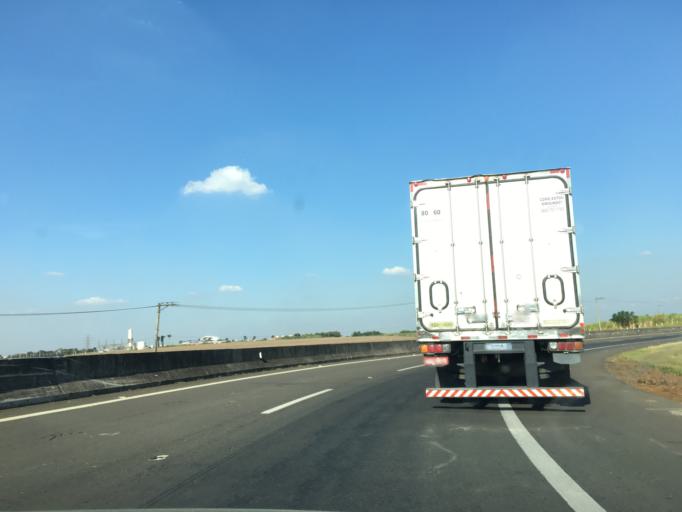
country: BR
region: Sao Paulo
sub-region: Santa Barbara D'Oeste
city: Santa Barbara d'Oeste
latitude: -22.7636
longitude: -47.4441
